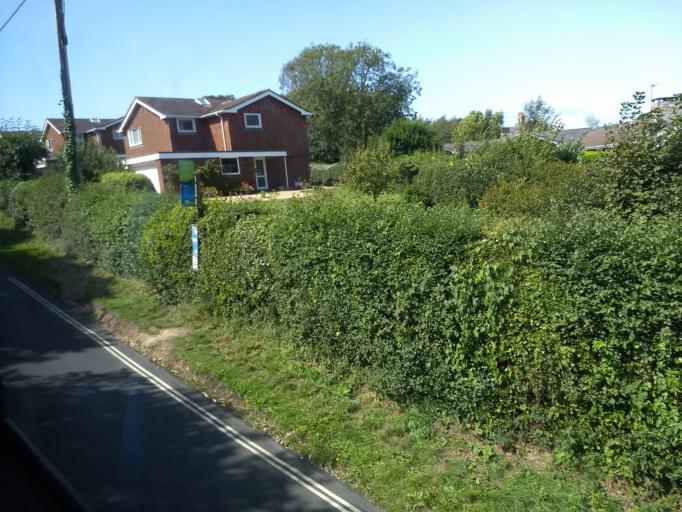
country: GB
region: England
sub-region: Isle of Wight
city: Totland
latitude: 50.6762
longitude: -1.5454
